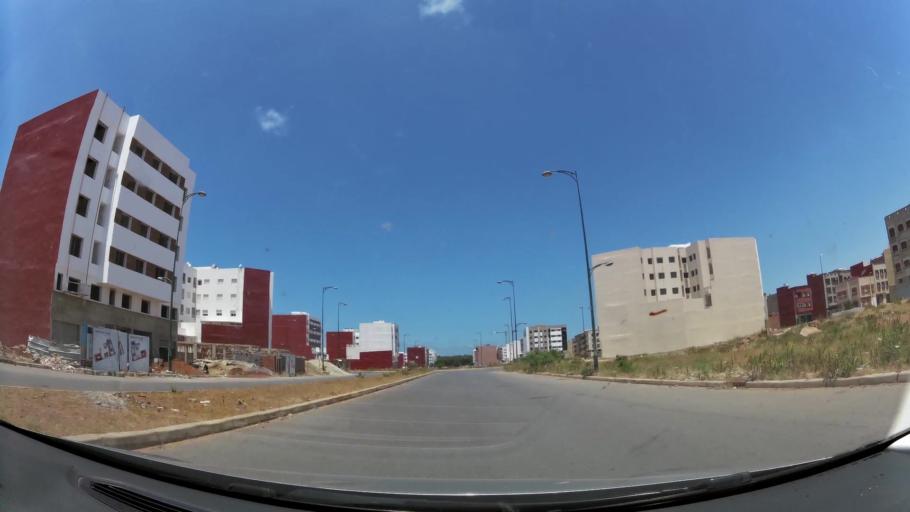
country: MA
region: Gharb-Chrarda-Beni Hssen
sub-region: Kenitra Province
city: Kenitra
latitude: 34.2665
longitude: -6.6265
